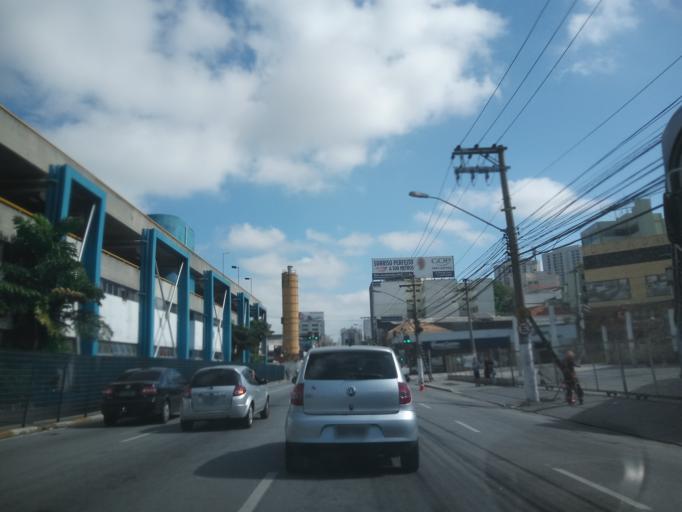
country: BR
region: Sao Paulo
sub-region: Sao Bernardo Do Campo
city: Sao Bernardo do Campo
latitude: -23.6985
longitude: -46.5535
